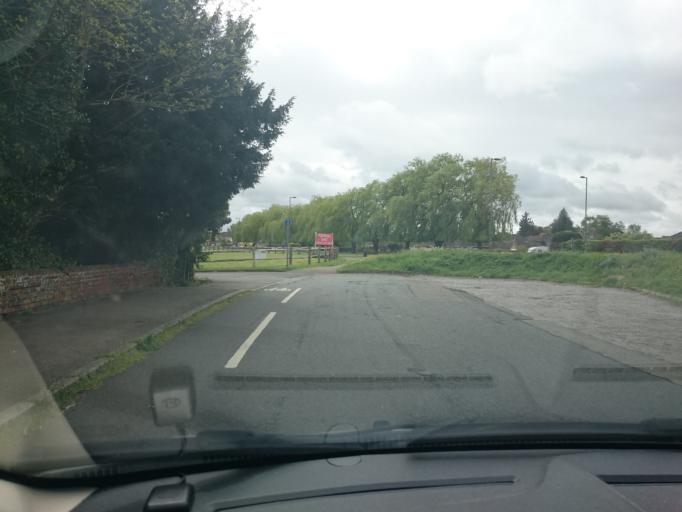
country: GB
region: England
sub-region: Surrey
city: Pirbright
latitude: 51.2653
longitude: -0.6185
